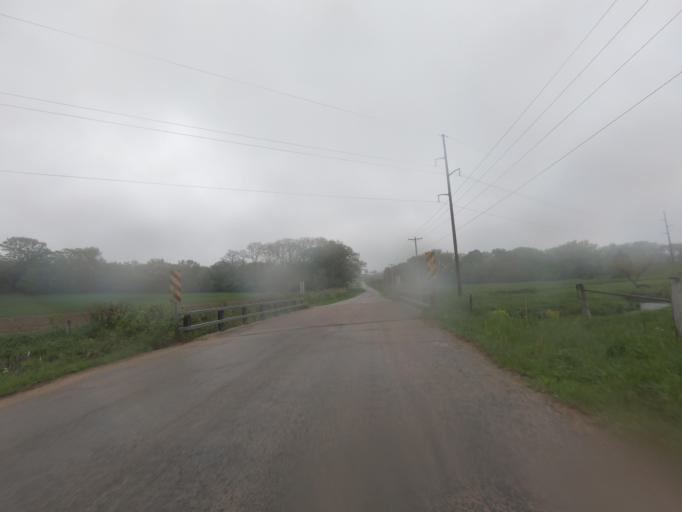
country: US
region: Wisconsin
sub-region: Grant County
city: Hazel Green
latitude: 42.5112
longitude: -90.5220
